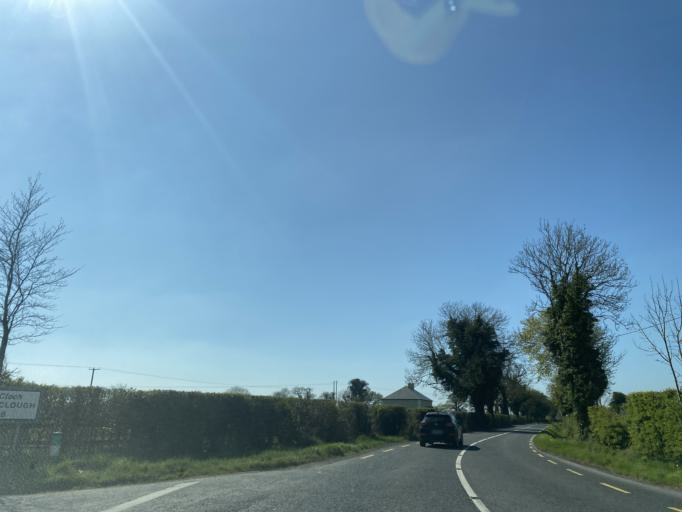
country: IE
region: Leinster
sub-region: Kildare
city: Kill
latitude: 53.2960
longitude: -6.6039
